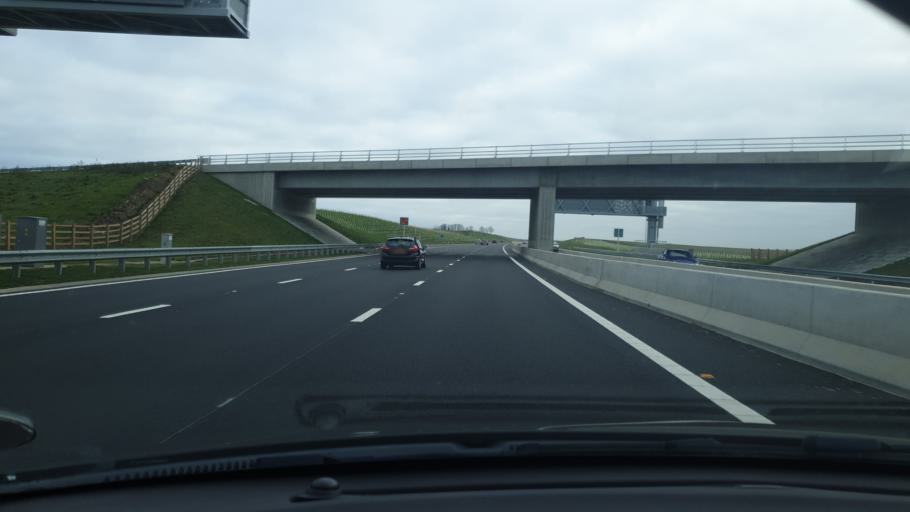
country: GB
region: England
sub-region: Cambridgeshire
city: Brampton
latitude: 52.2992
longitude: -0.2035
